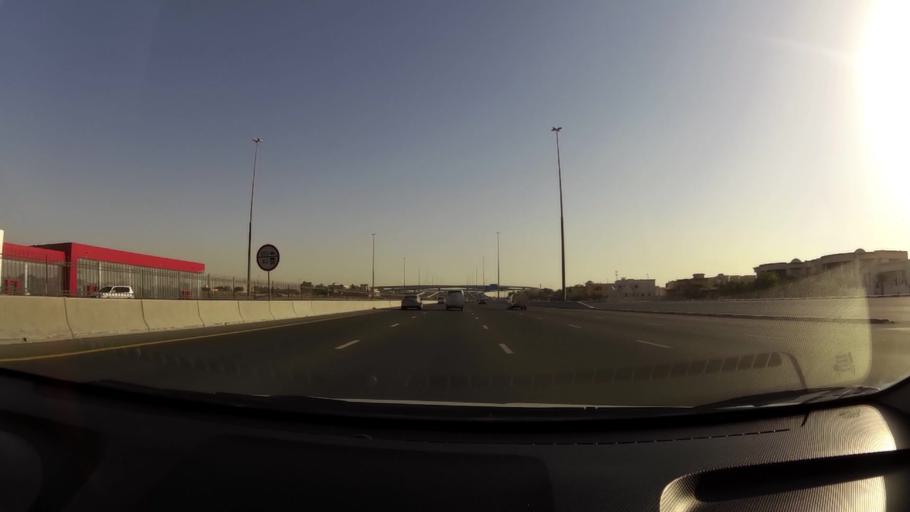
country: AE
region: Ash Shariqah
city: Sharjah
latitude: 25.3419
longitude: 55.4705
